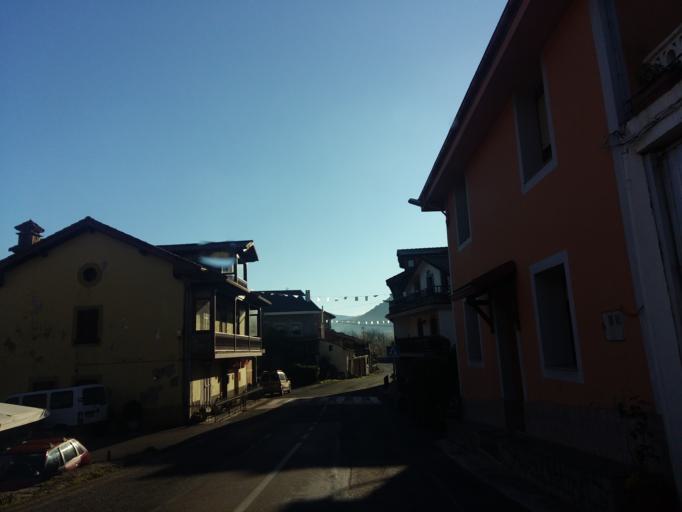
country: ES
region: Cantabria
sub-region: Provincia de Cantabria
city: Ramales de la Victoria
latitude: 43.2785
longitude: -3.5267
